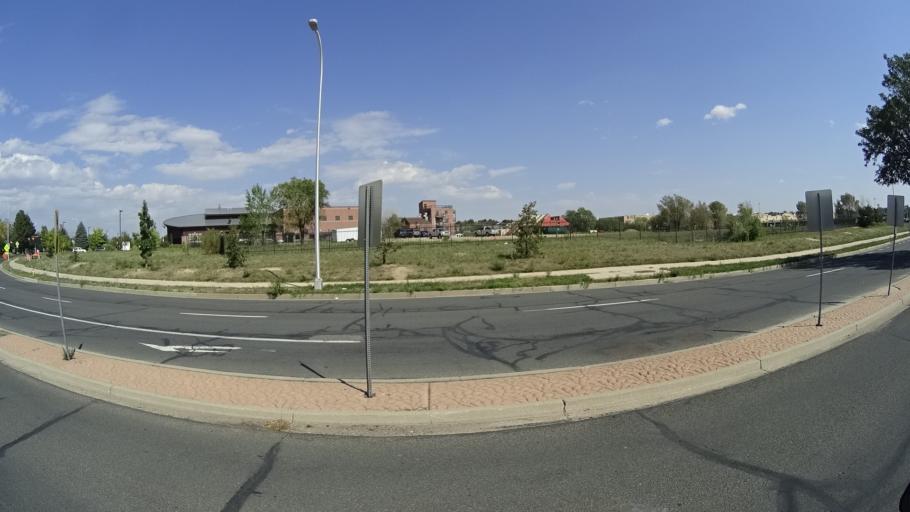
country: US
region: Colorado
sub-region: El Paso County
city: Colorado Springs
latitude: 38.8253
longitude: -104.7849
